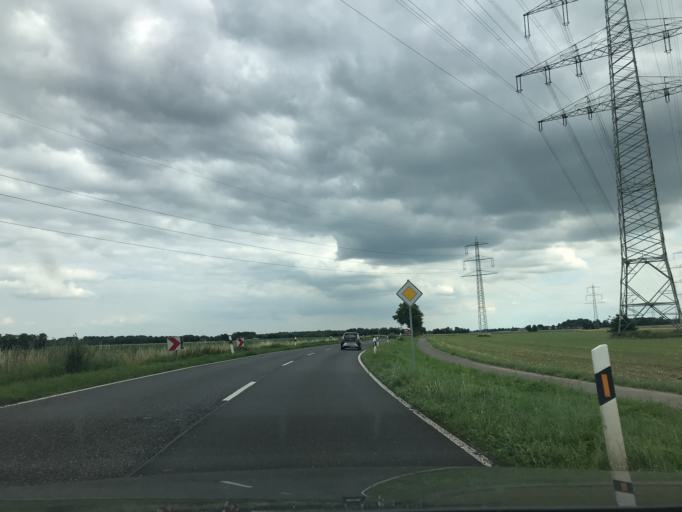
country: DE
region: North Rhine-Westphalia
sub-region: Regierungsbezirk Dusseldorf
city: Neubrueck
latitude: 51.1303
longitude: 6.6922
